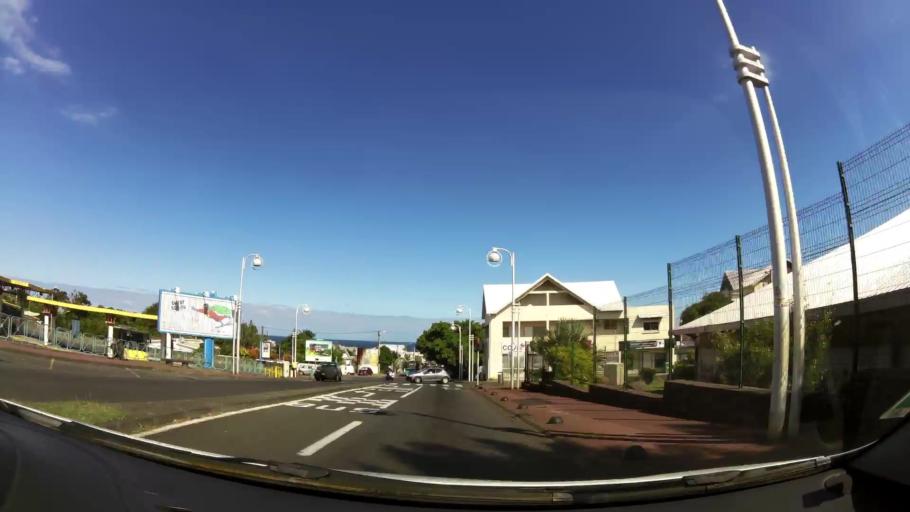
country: RE
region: Reunion
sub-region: Reunion
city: Saint-Pierre
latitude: -21.3339
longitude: 55.4712
